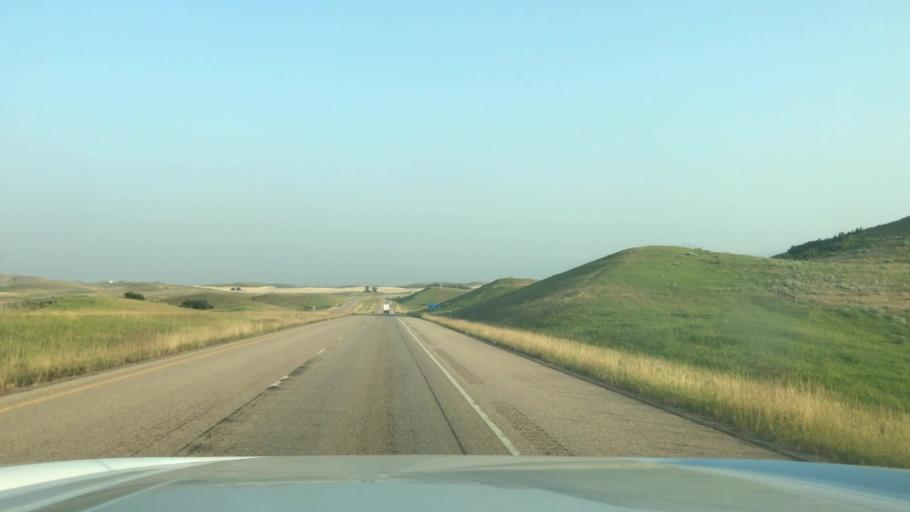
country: US
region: Wyoming
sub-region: Sheridan County
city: Sheridan
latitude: 45.0172
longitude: -107.3077
